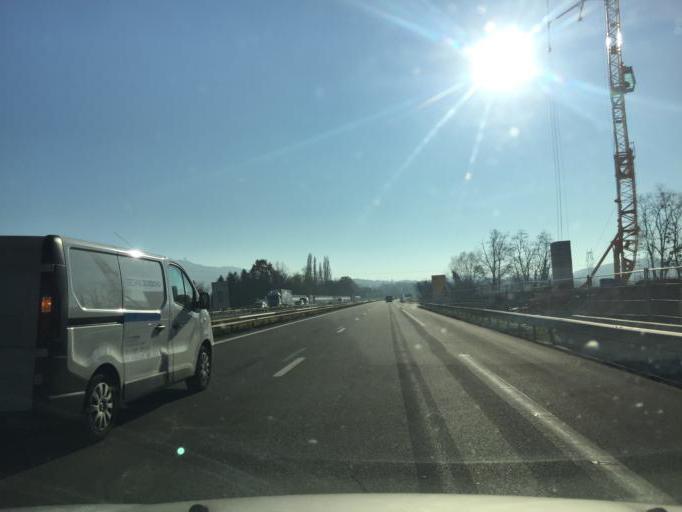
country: FR
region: Rhone-Alpes
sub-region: Departement du Rhone
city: Les Cheres
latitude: 45.8864
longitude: 4.7365
